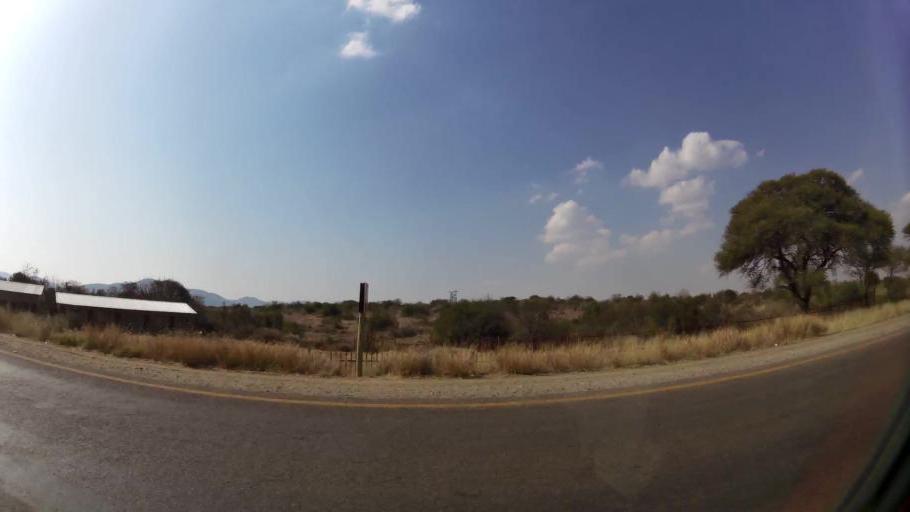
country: ZA
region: North-West
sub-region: Bojanala Platinum District Municipality
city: Mogwase
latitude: -25.3854
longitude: 27.0686
